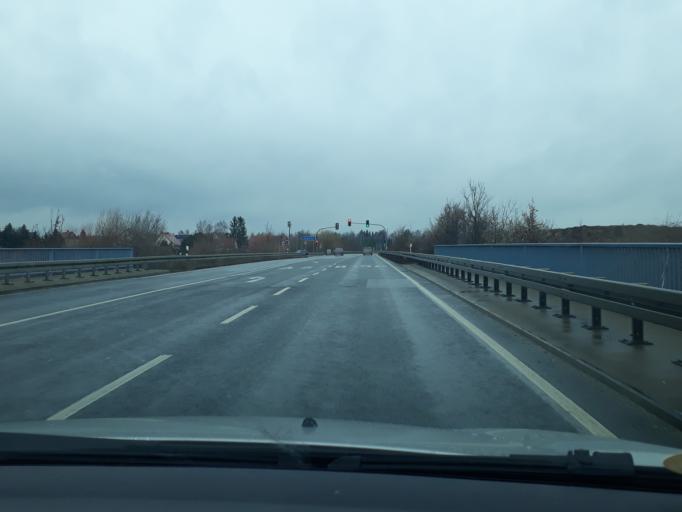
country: DE
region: Saxony
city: Bautzen
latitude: 51.1956
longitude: 14.4654
